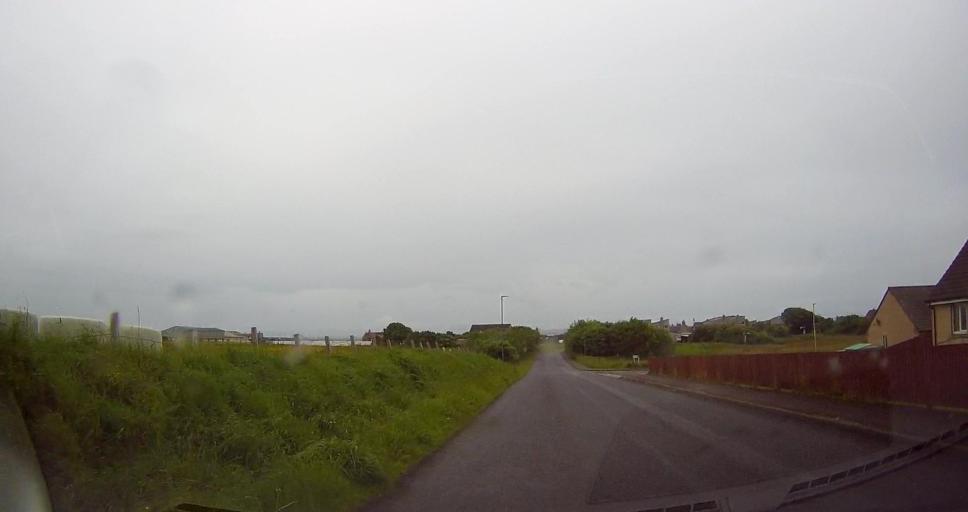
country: GB
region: Scotland
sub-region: Orkney Islands
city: Stromness
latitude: 59.0703
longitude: -3.2273
